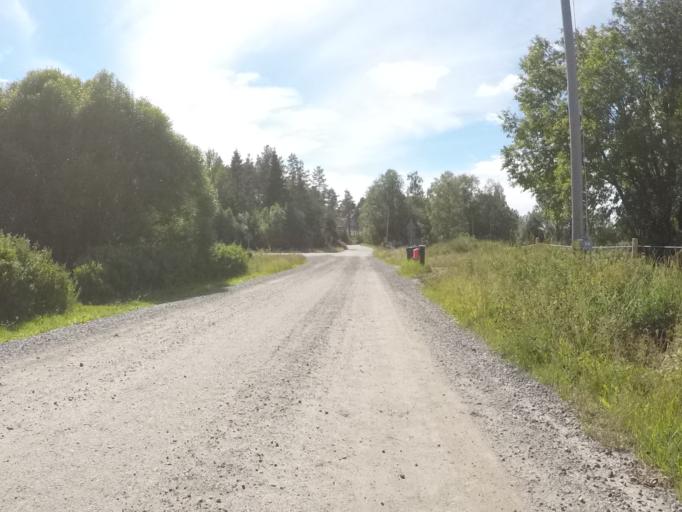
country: SE
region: Vaesterbotten
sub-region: Robertsfors Kommun
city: Robertsfors
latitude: 63.9996
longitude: 20.8108
